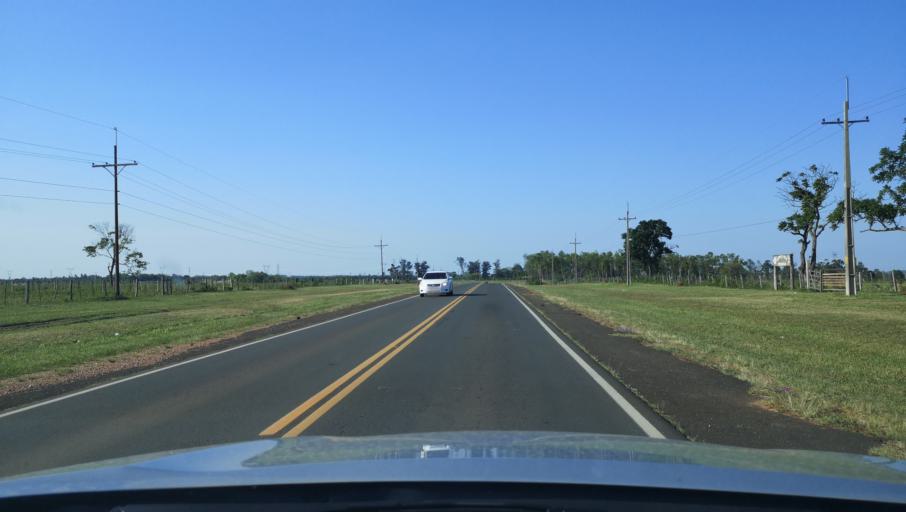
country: PY
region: Misiones
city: Santa Maria
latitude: -26.8120
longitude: -57.0219
